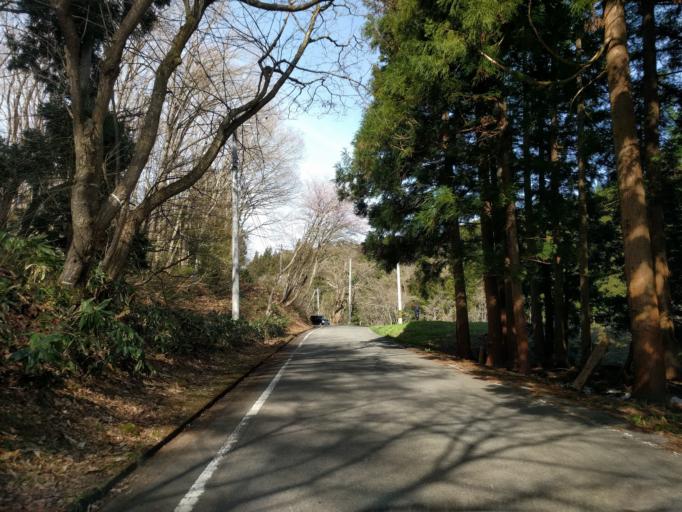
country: JP
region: Fukushima
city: Inawashiro
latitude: 37.5216
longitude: 140.0401
